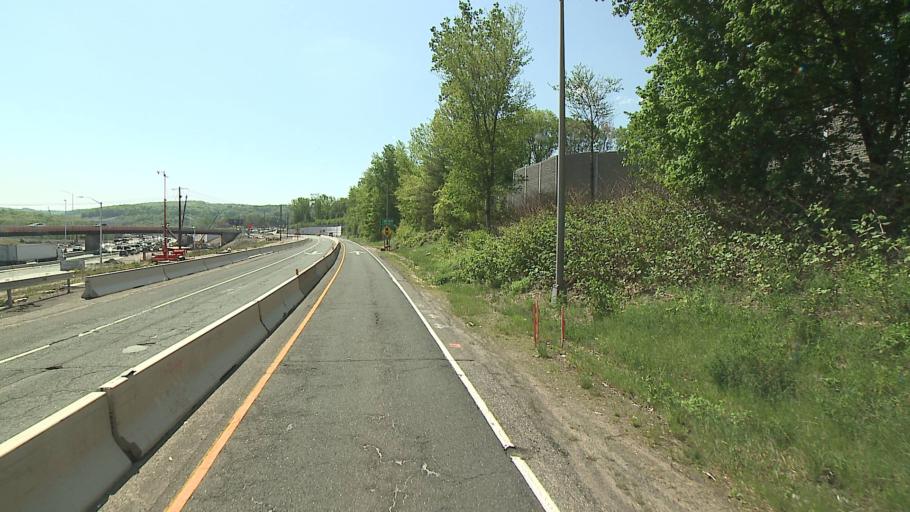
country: US
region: Connecticut
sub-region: New Haven County
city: Waterbury
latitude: 41.5429
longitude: -73.0253
